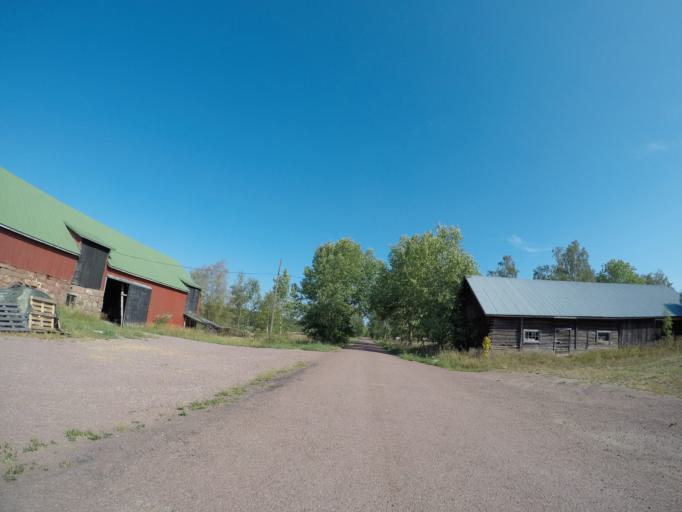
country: AX
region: Alands landsbygd
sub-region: Finstroem
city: Finstroem
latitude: 60.2779
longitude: 19.9572
